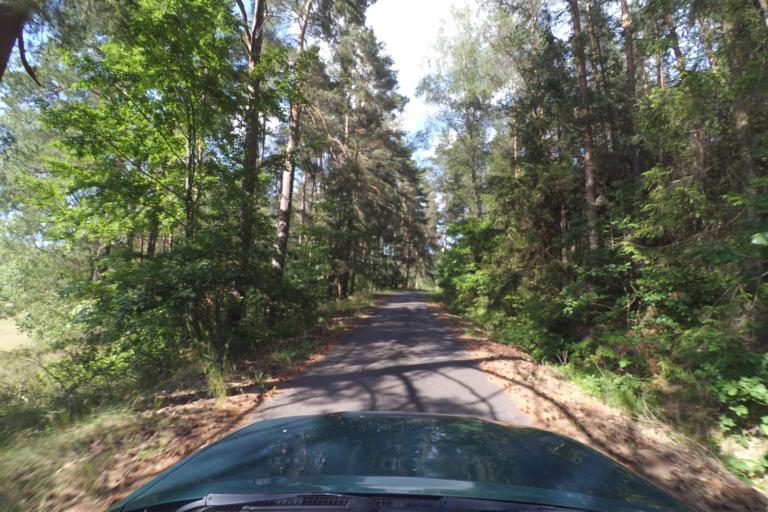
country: CZ
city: Osecna
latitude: 50.6770
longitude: 14.8897
